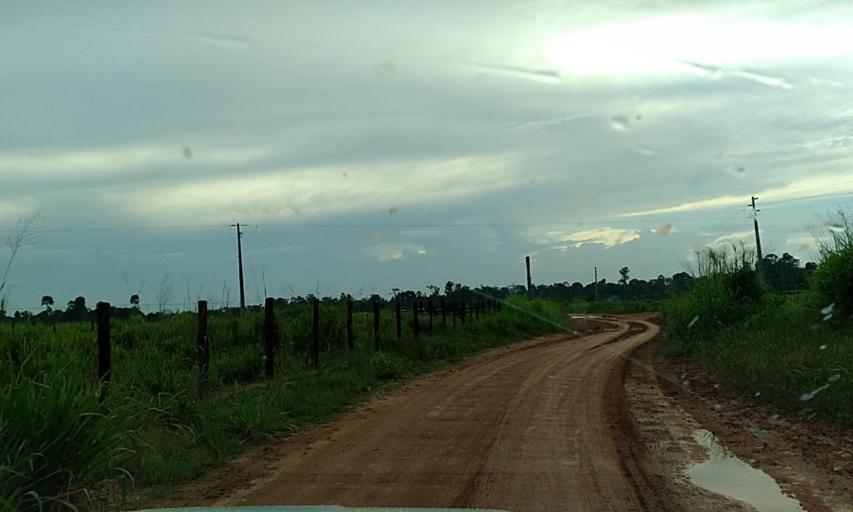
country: BR
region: Para
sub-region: Senador Jose Porfirio
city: Senador Jose Porfirio
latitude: -2.5593
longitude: -51.8797
